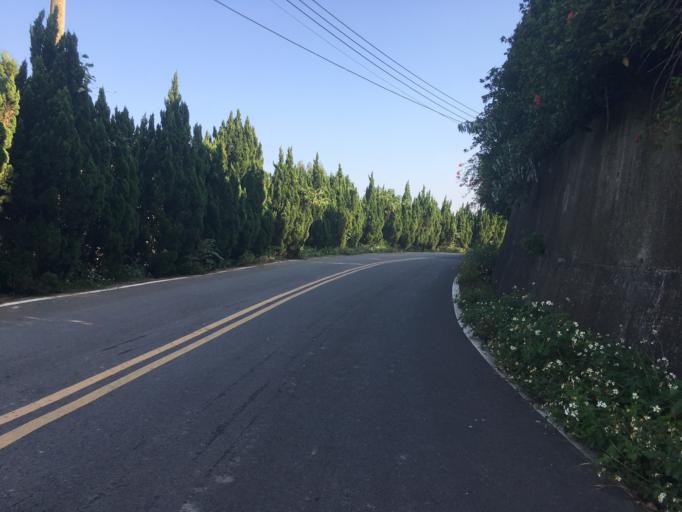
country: TW
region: Taiwan
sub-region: Hsinchu
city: Hsinchu
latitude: 24.7320
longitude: 120.9887
